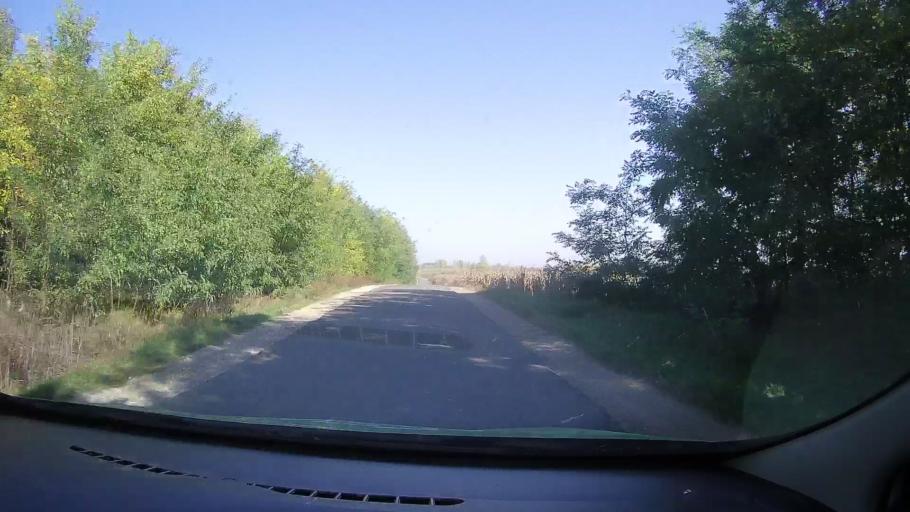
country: RO
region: Satu Mare
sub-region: Comuna Ciumesti
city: Ciumesti
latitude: 47.6898
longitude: 22.3547
